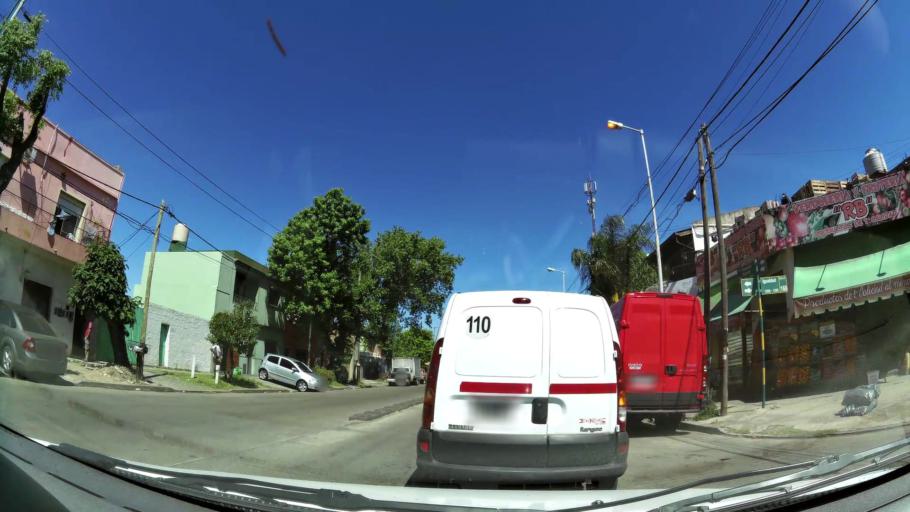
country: AR
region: Buenos Aires
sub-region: Partido de General San Martin
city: General San Martin
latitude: -34.5268
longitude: -58.5579
